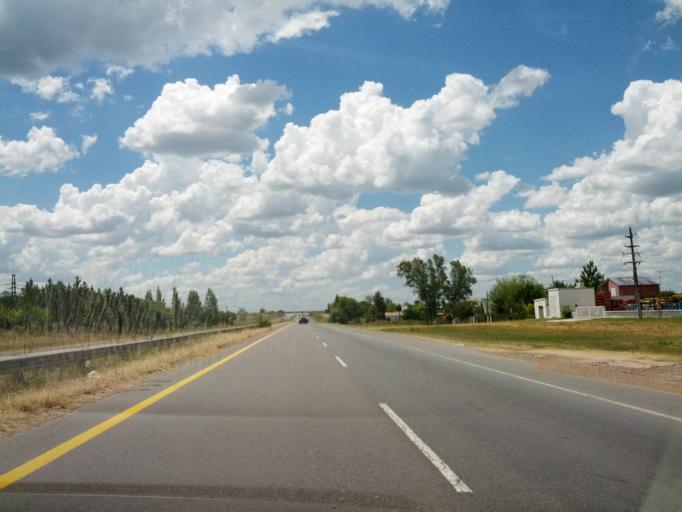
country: AR
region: Entre Rios
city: Gualeguaychu
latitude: -33.0476
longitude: -58.6217
